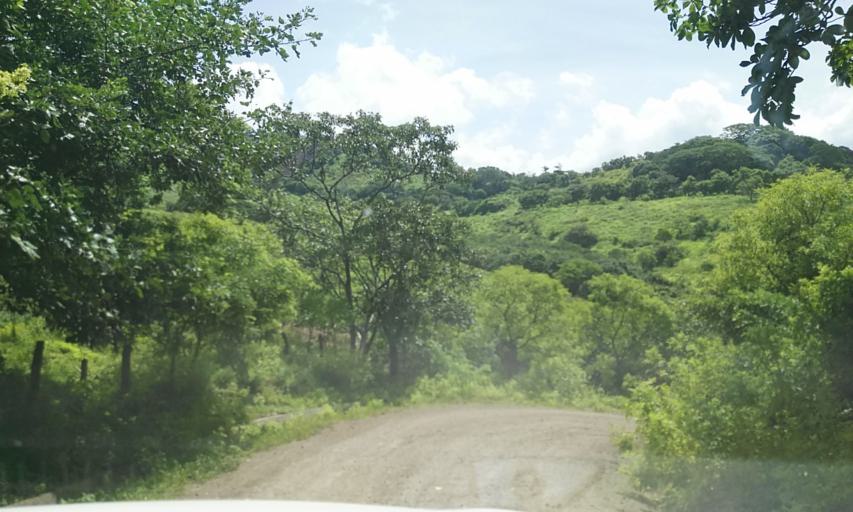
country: NI
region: Matagalpa
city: Terrabona
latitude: 12.7004
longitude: -85.9360
